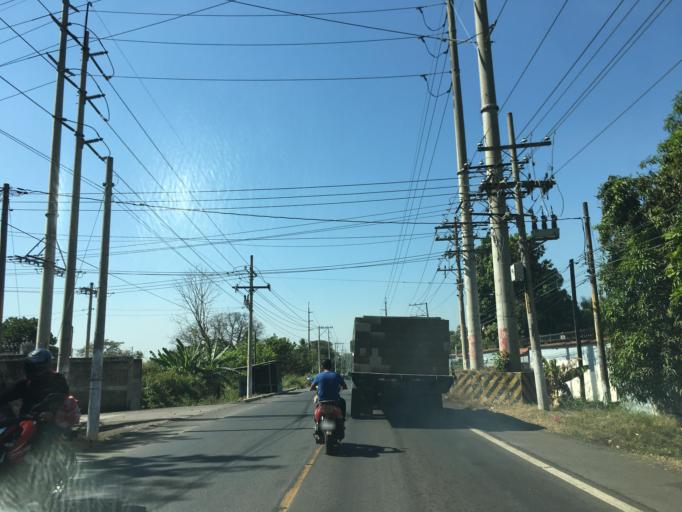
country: GT
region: Escuintla
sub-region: Municipio de Masagua
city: Masagua
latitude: 14.2065
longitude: -90.8417
